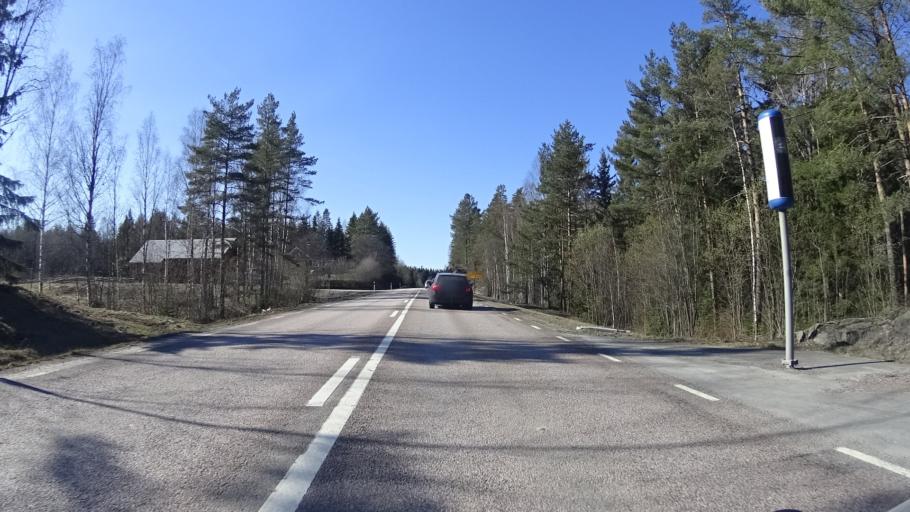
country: SE
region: Vaermland
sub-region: Karlstads Kommun
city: Edsvalla
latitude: 59.5434
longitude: 13.0755
